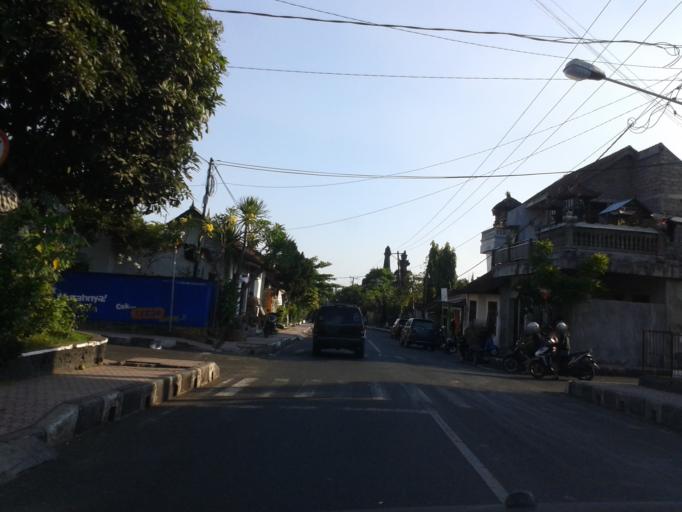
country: ID
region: Bali
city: Semarapura
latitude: -8.5327
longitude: 115.4041
